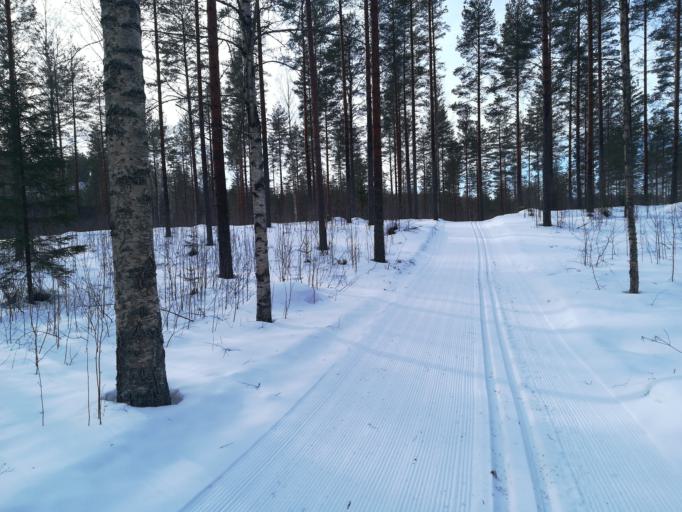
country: FI
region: Southern Savonia
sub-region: Savonlinna
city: Savonlinna
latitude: 61.8075
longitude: 29.0528
